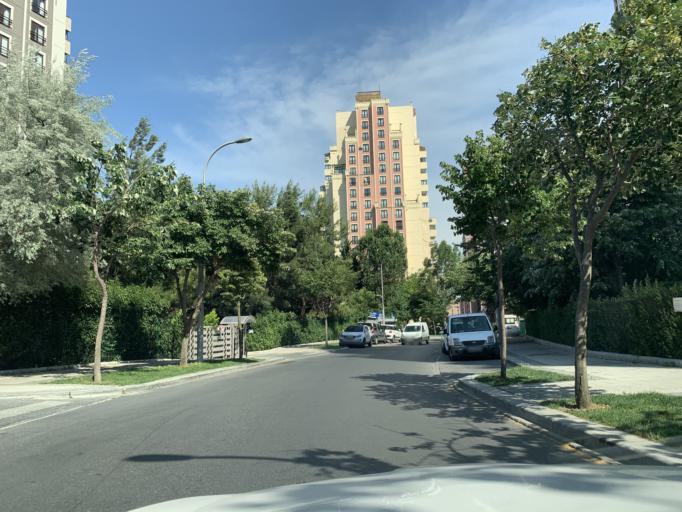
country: TR
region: Istanbul
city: Esenyurt
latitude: 41.0663
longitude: 28.6807
